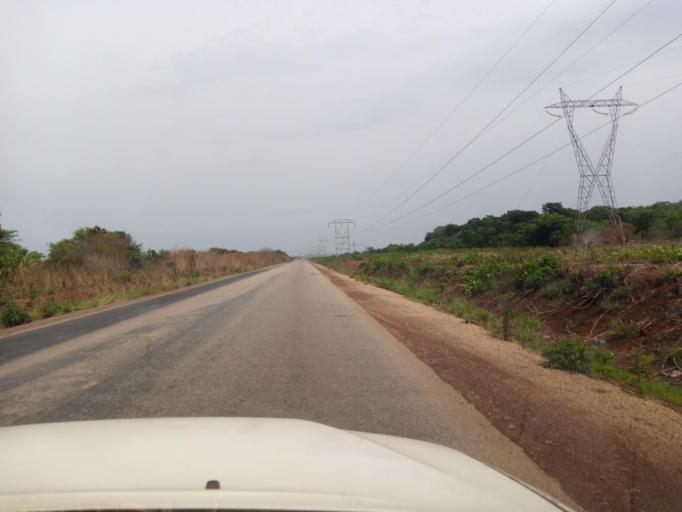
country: CD
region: Katanga
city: Likasi
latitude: -11.0700
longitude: 26.9841
